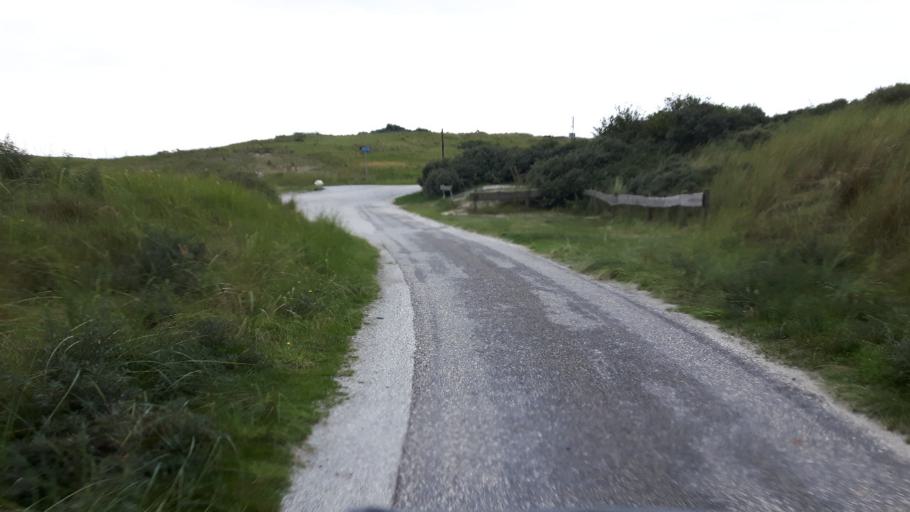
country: NL
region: Friesland
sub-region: Gemeente Ameland
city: Nes
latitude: 53.4609
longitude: 5.8351
